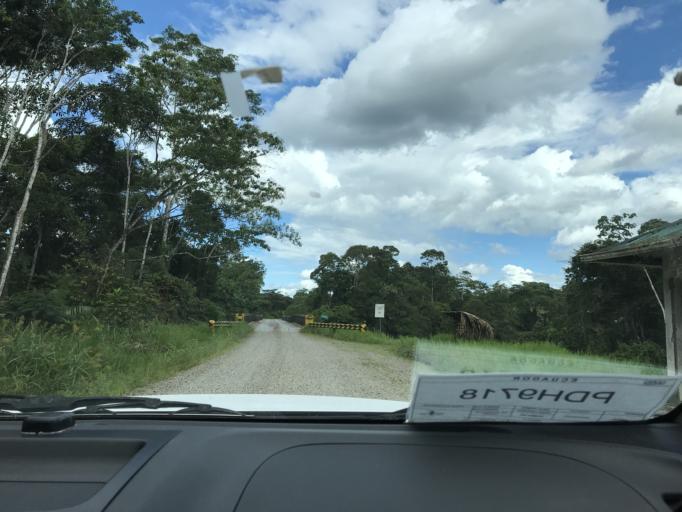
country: EC
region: Orellana
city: Puerto Francisco de Orellana
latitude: -0.6083
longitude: -76.4685
